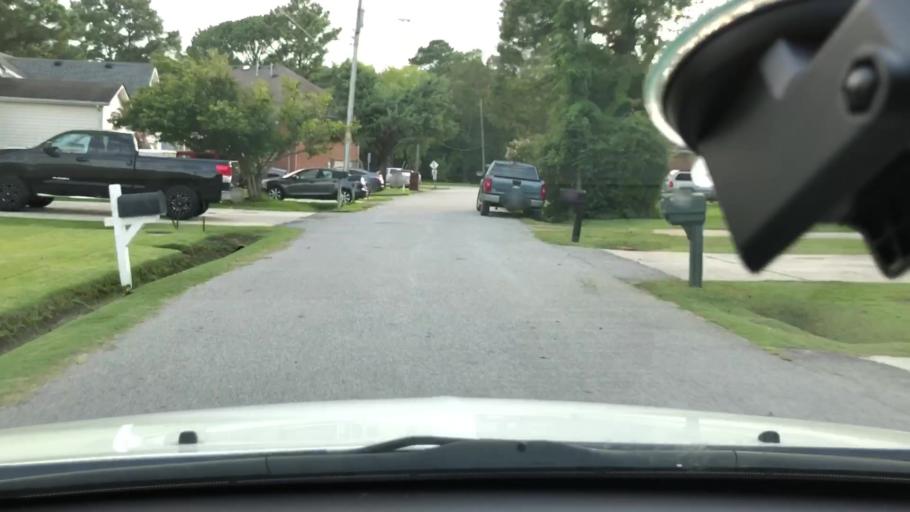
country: US
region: Virginia
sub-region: City of Chesapeake
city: Chesapeake
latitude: 36.7183
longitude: -76.2647
